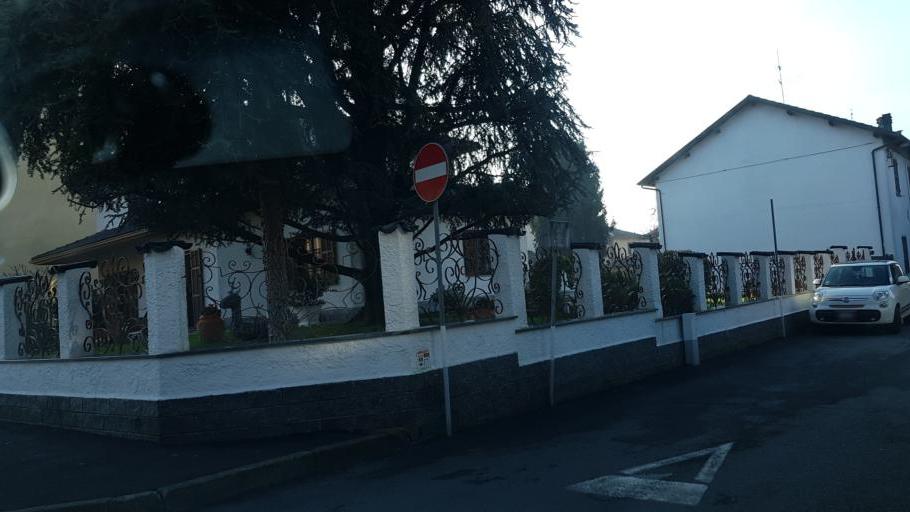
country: IT
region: Piedmont
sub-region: Provincia di Alessandria
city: Novi Ligure
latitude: 44.7702
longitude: 8.7914
